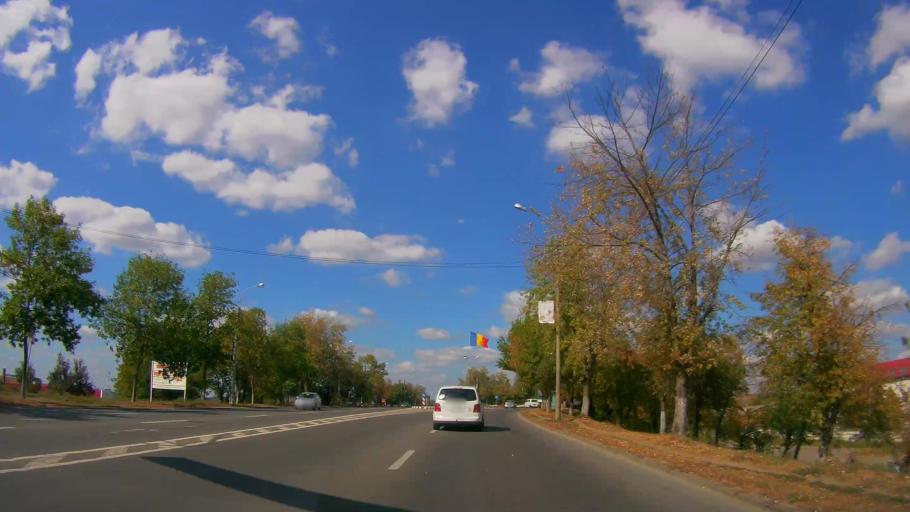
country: RO
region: Salaj
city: Zalau
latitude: 47.2157
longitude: 23.0423
